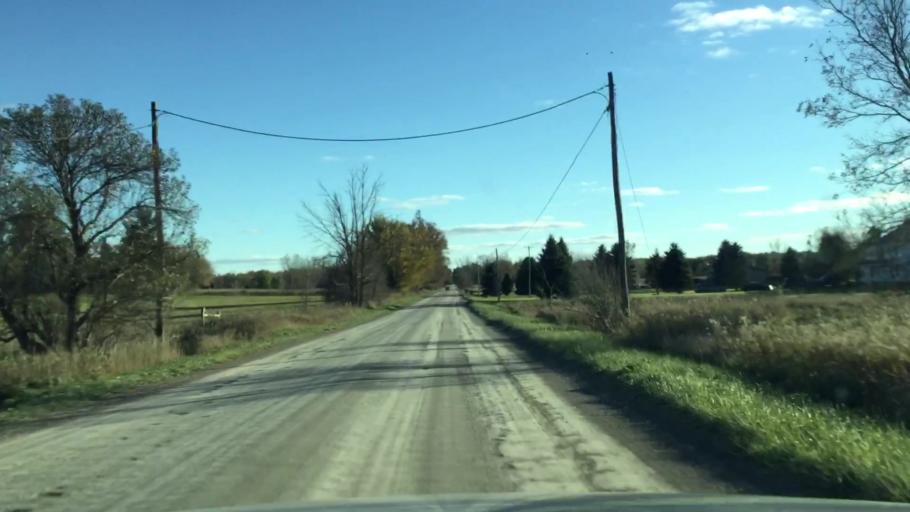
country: US
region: Michigan
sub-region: Lapeer County
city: Lapeer
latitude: 43.0661
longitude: -83.2270
